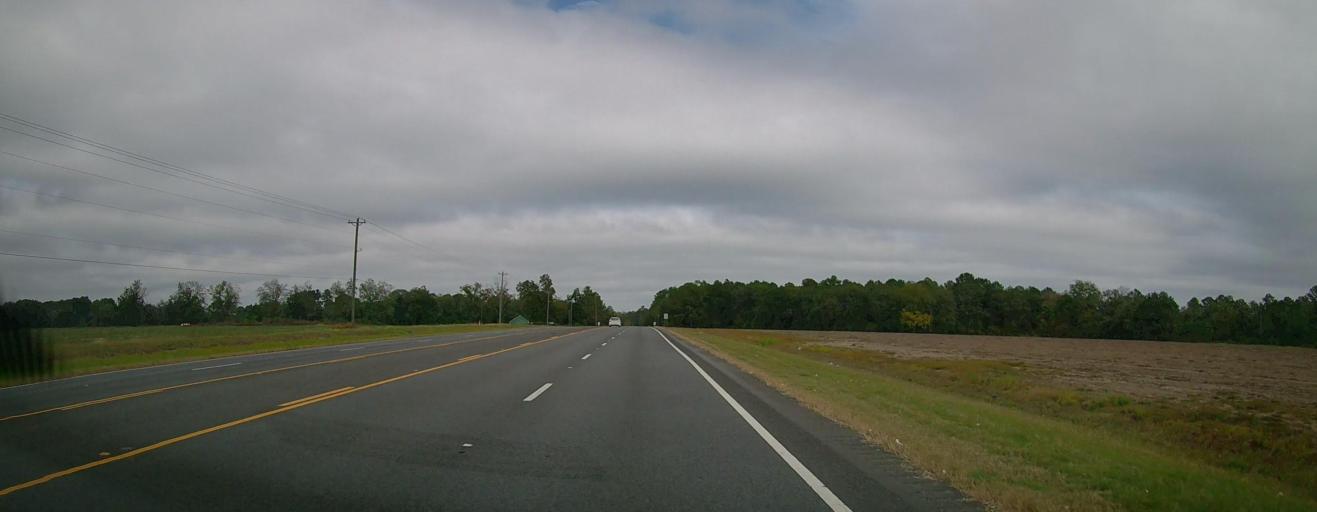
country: US
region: Georgia
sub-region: Thomas County
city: Thomasville
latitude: 30.9952
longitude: -83.8735
